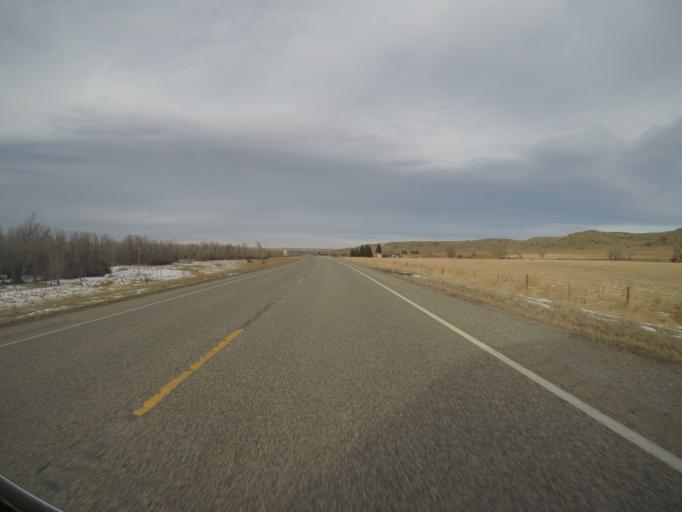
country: US
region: Montana
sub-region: Stillwater County
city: Absarokee
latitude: 45.4682
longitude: -109.4479
